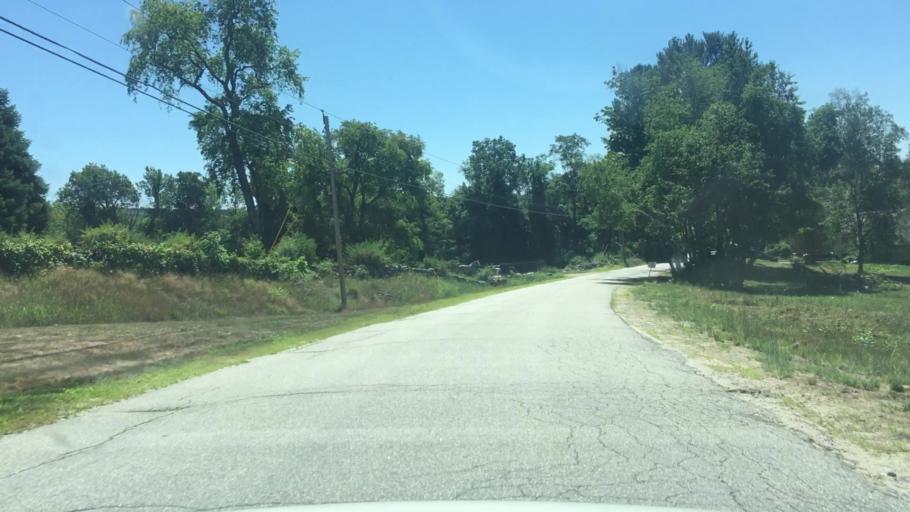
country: US
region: New Hampshire
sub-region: Merrimack County
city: Hopkinton
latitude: 43.2179
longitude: -71.6733
